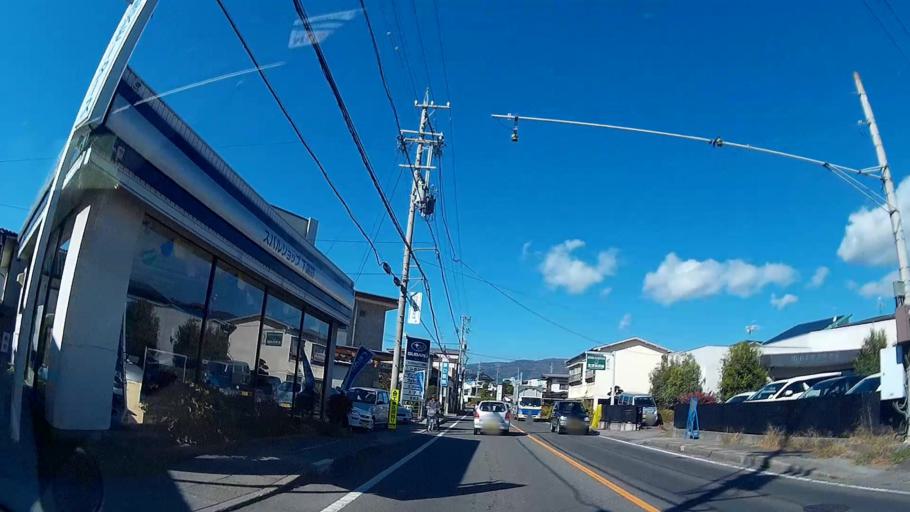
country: JP
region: Nagano
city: Suwa
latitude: 36.0705
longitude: 138.0939
